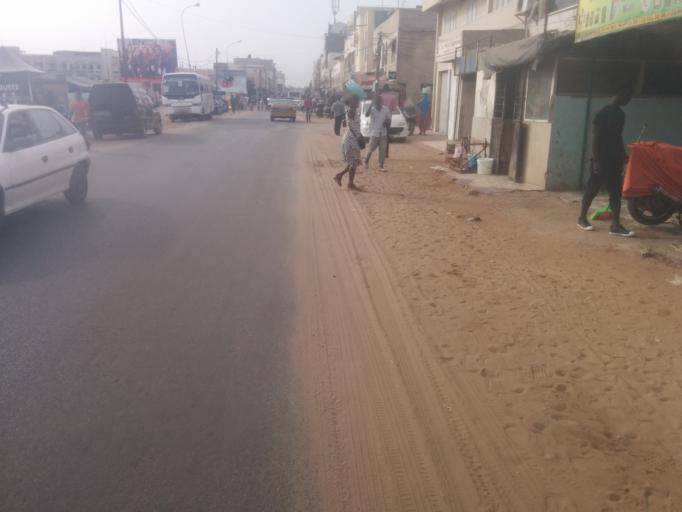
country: SN
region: Dakar
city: Grand Dakar
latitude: 14.7567
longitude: -17.4474
